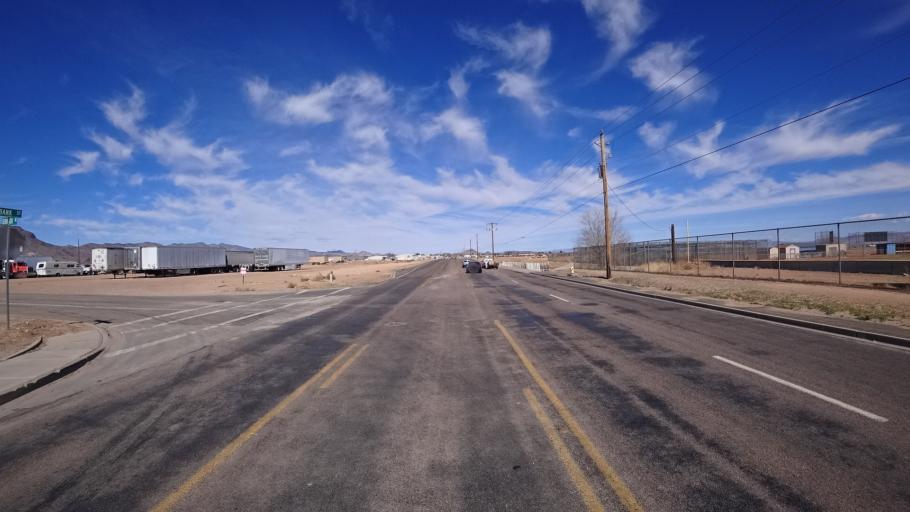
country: US
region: Arizona
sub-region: Mohave County
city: New Kingman-Butler
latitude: 35.2465
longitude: -114.0116
